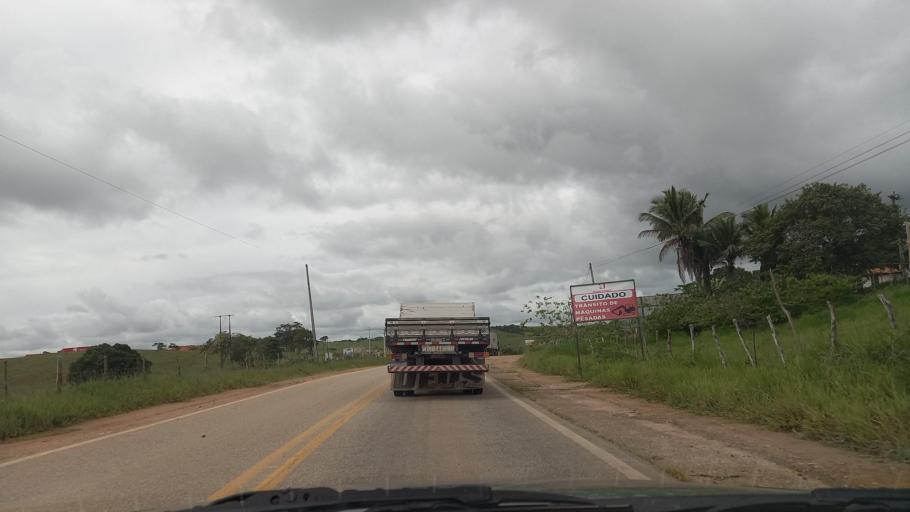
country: BR
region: Pernambuco
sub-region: Canhotinho
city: Canhotinho
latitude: -8.8548
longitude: -36.1721
